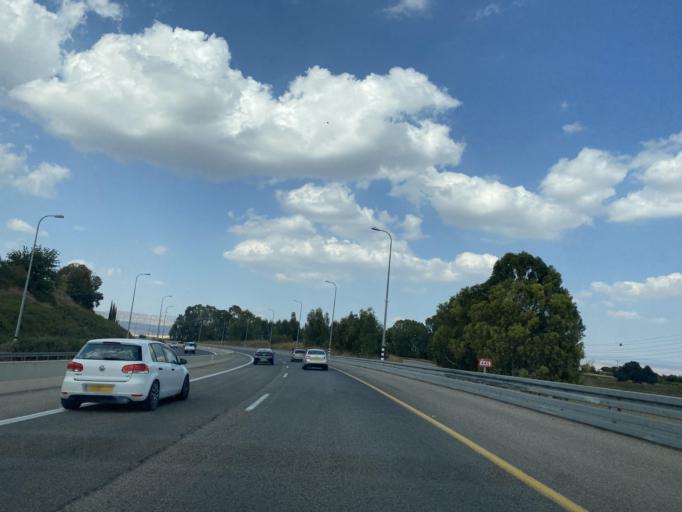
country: IL
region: Northern District
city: Rosh Pinna
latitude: 33.0010
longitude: 35.5658
